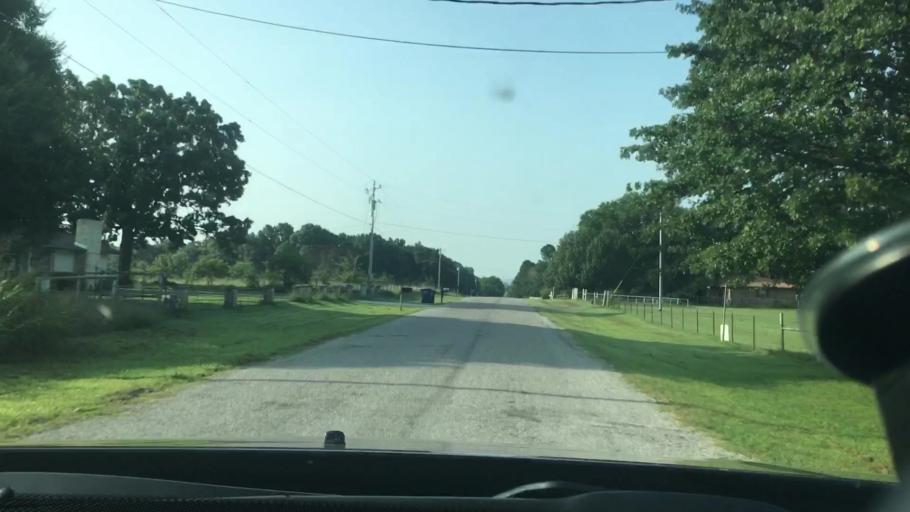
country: US
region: Oklahoma
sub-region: Pontotoc County
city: Ada
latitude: 34.7967
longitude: -96.7397
